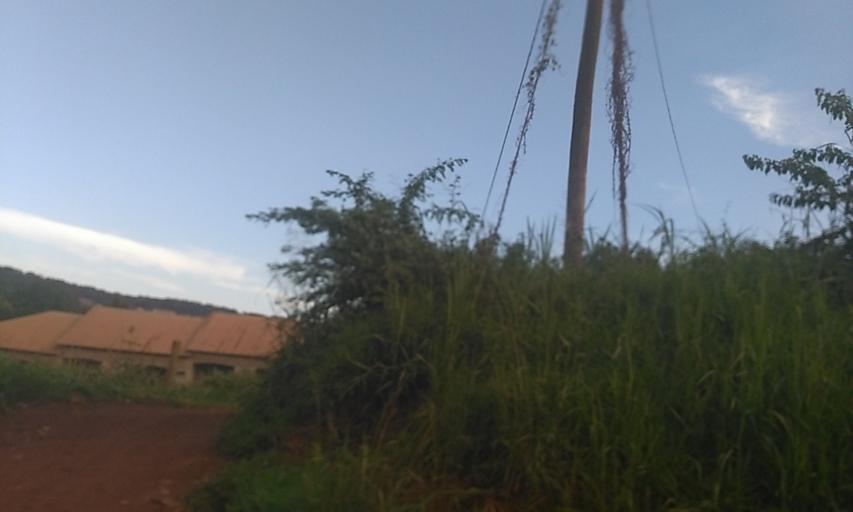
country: UG
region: Central Region
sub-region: Wakiso District
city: Kajansi
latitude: 0.2411
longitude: 32.4974
